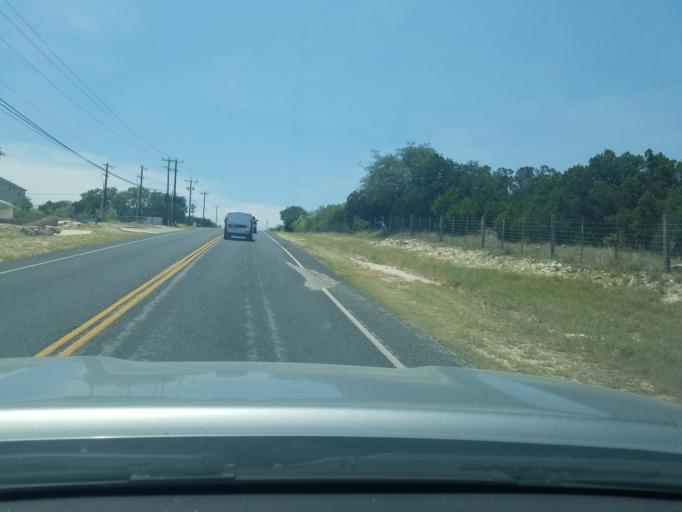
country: US
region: Texas
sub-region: Bexar County
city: Timberwood Park
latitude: 29.6625
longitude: -98.4370
